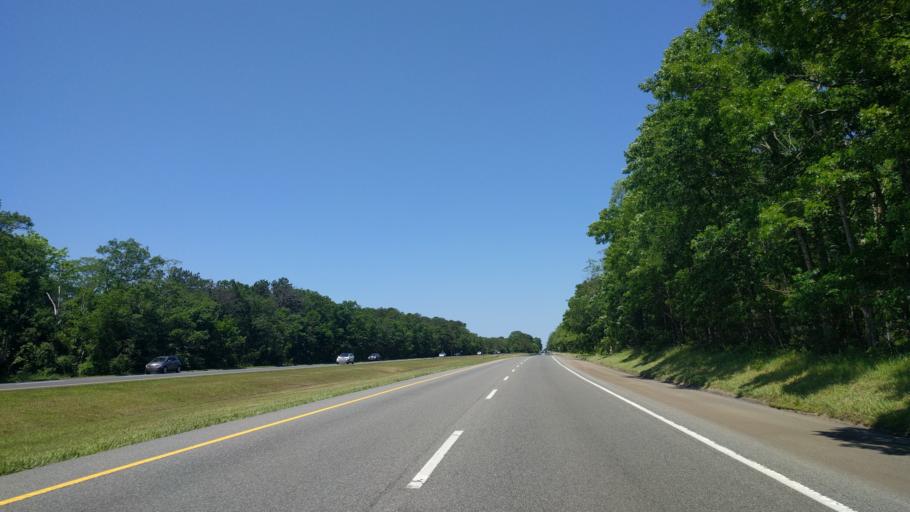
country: US
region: New York
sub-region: Suffolk County
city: Eastport
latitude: 40.8521
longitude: -72.7494
